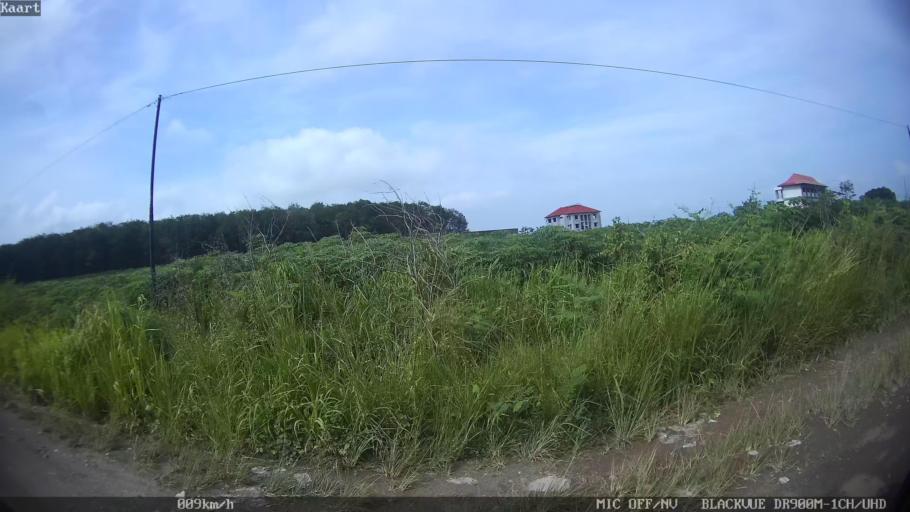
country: ID
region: Lampung
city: Kedaton
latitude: -5.3738
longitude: 105.3200
